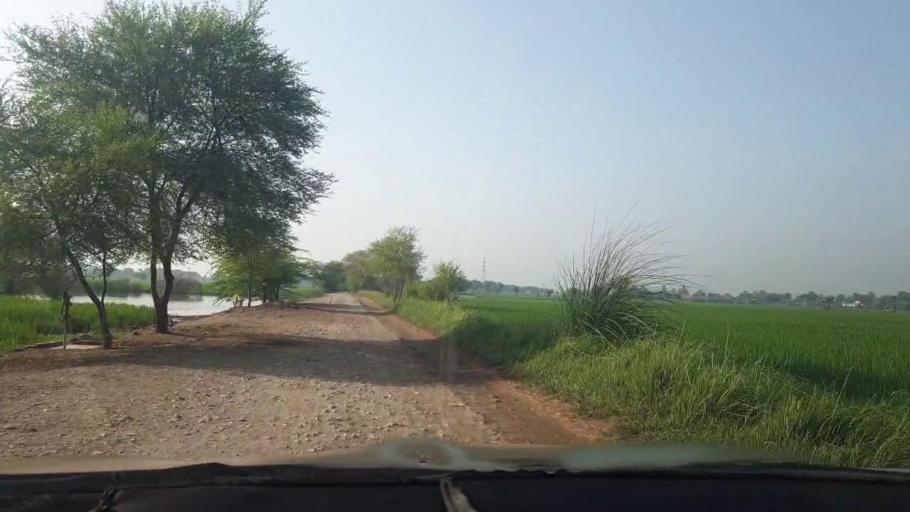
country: PK
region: Sindh
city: Kambar
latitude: 27.5779
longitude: 68.1021
